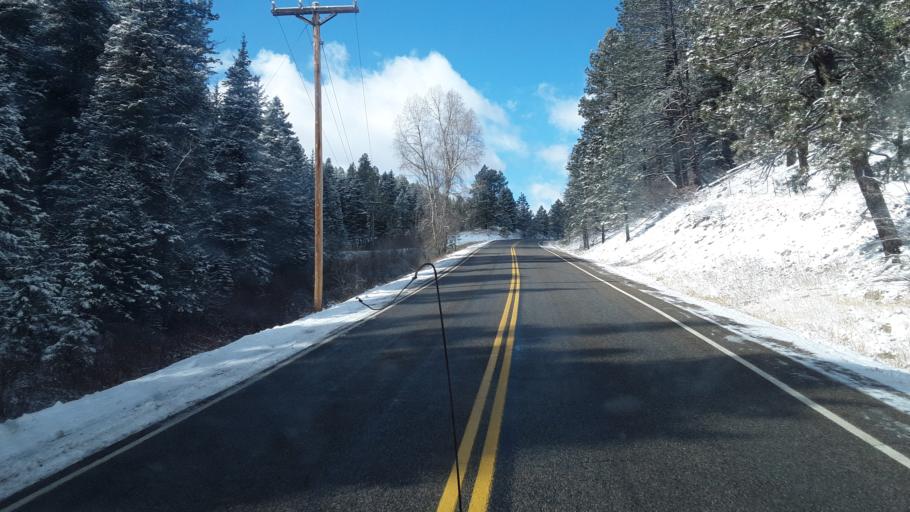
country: US
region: Colorado
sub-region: La Plata County
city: Bayfield
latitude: 37.3535
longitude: -107.6534
